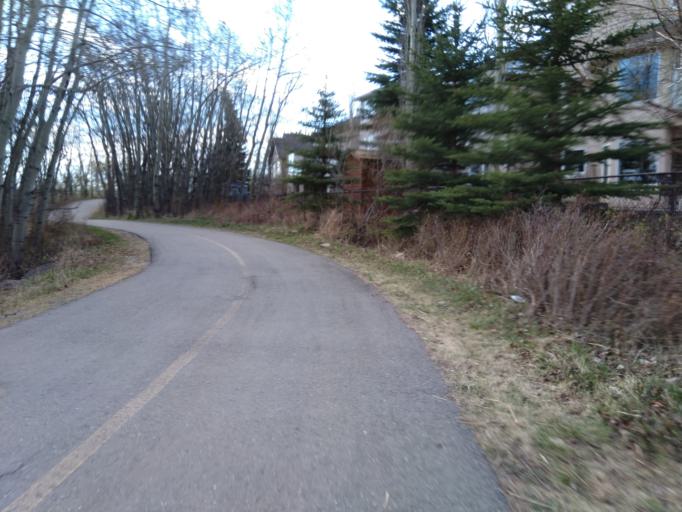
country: CA
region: Alberta
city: Calgary
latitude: 51.1192
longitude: -114.2371
